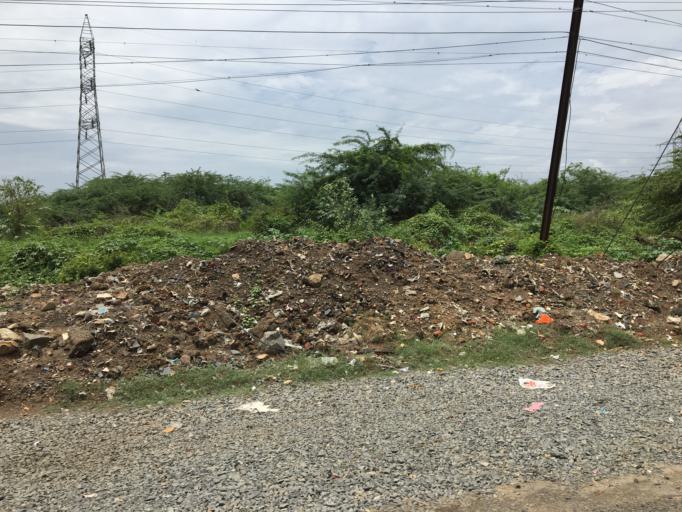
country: IN
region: Tamil Nadu
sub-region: Kancheepuram
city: Madipakkam
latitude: 12.9606
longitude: 80.2149
